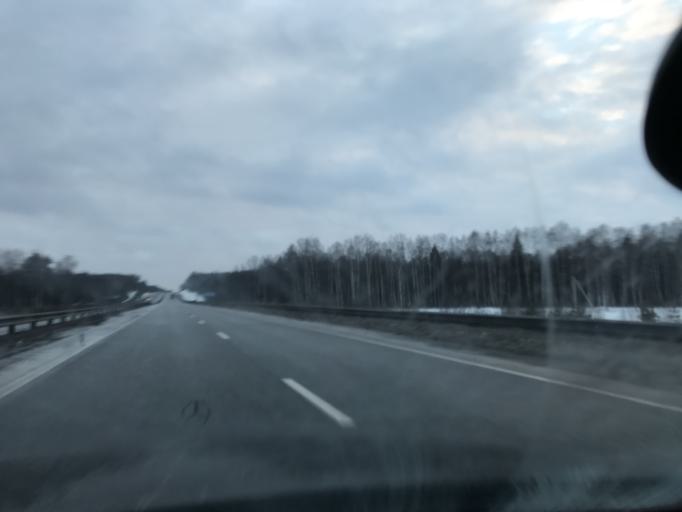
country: RU
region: Vladimir
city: Sudogda
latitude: 56.1251
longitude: 40.8658
